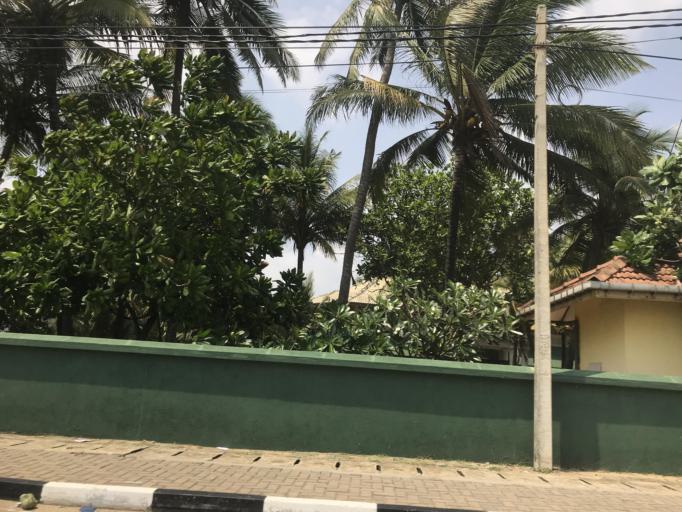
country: LK
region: Southern
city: Matara
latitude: 5.9426
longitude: 80.5548
